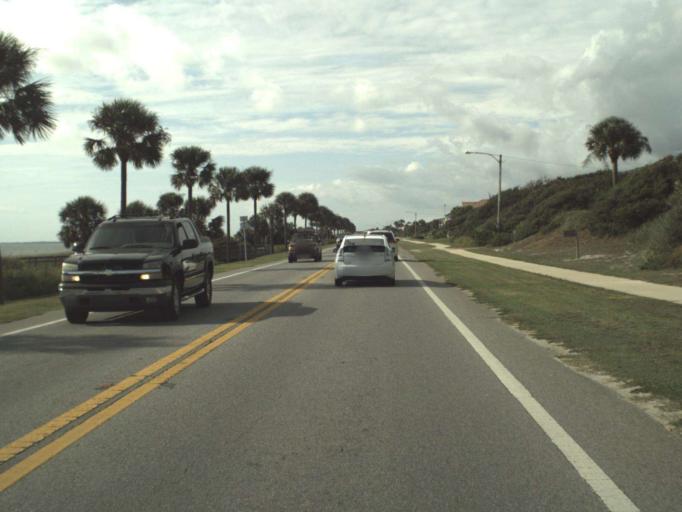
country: US
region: Florida
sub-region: Bay County
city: Mexico Beach
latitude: 29.9259
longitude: -85.3893
